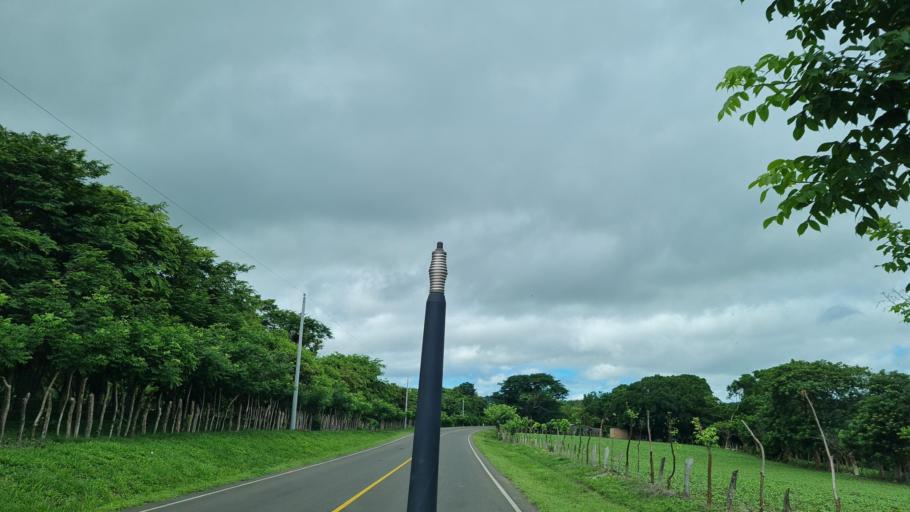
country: NI
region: Boaco
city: San Jose de los Remates
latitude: 12.6019
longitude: -85.8986
